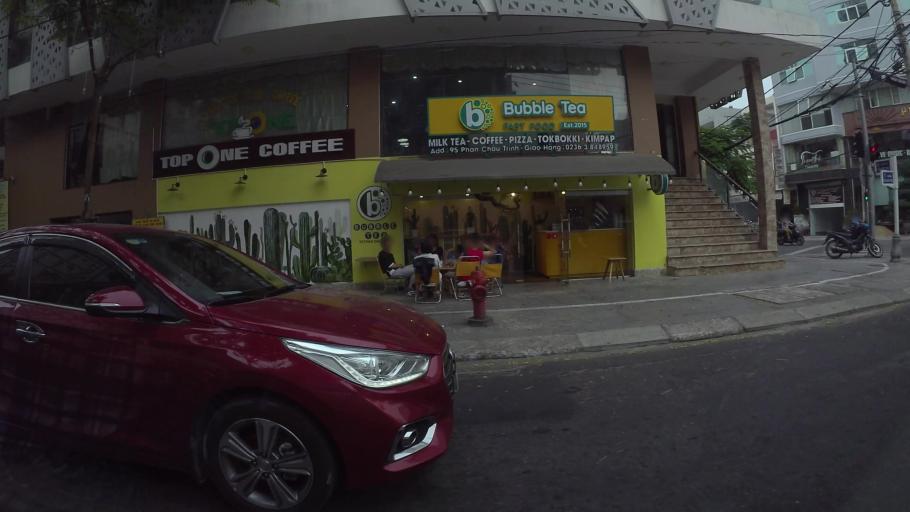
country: VN
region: Da Nang
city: Da Nang
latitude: 16.0665
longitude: 108.2202
